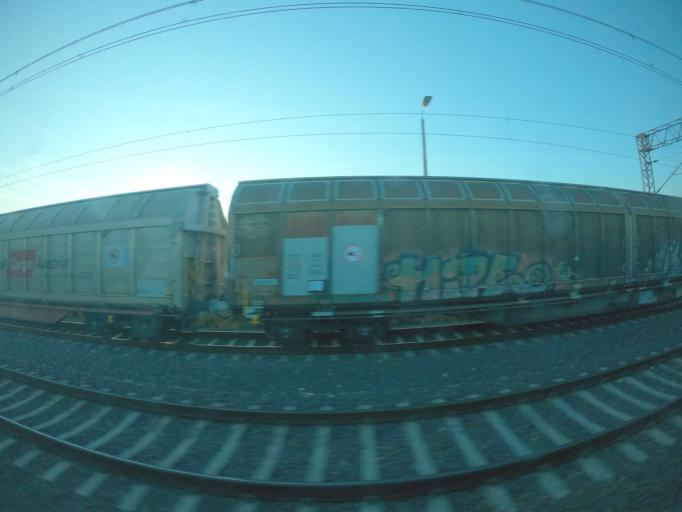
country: PL
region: Lubusz
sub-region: Powiat slubicki
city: Gorzyca
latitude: 52.5217
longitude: 14.6506
